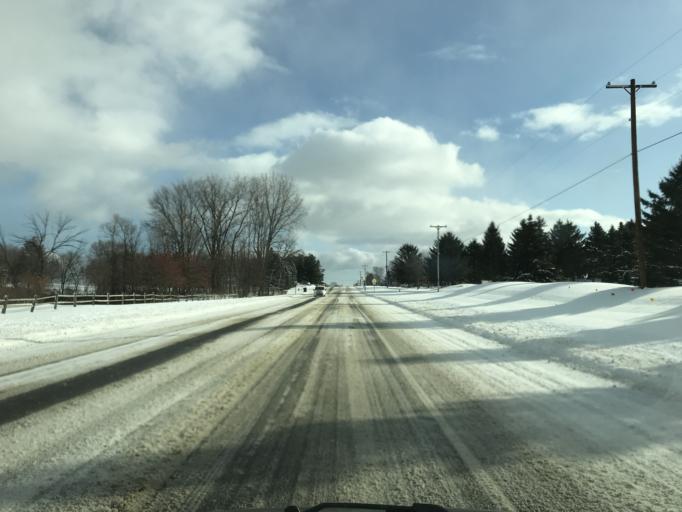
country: US
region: Michigan
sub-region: Kent County
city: Byron Center
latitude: 42.8268
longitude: -85.7294
